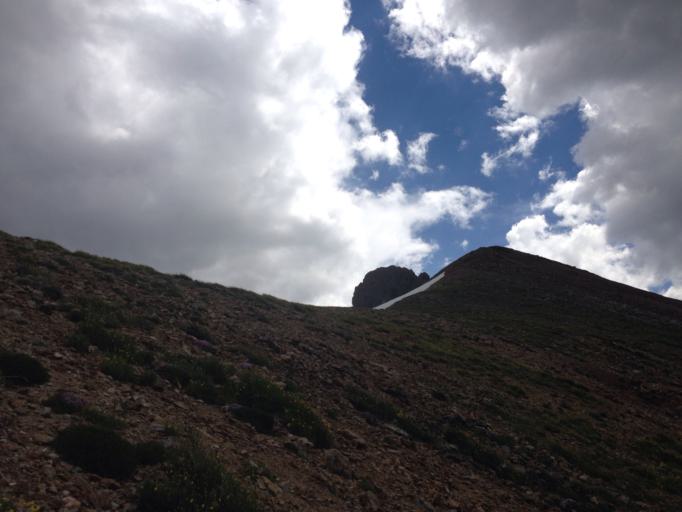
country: US
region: Colorado
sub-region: Larimer County
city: Estes Park
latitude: 40.4926
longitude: -105.8901
